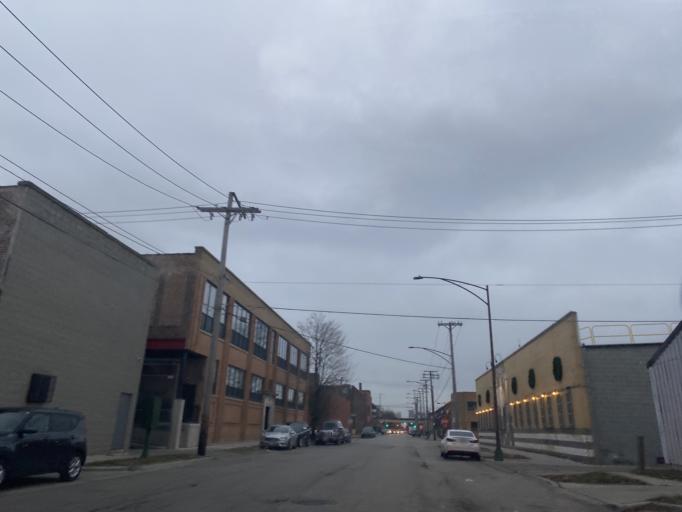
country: US
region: Illinois
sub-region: Cook County
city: Chicago
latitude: 41.8875
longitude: -87.6719
